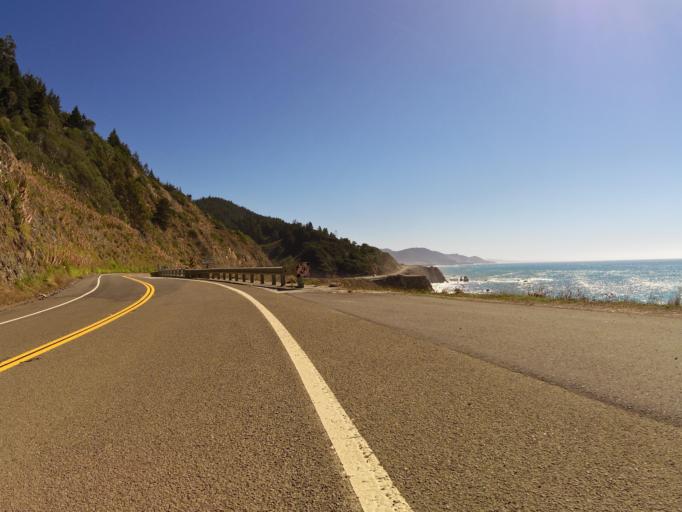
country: US
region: California
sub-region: Mendocino County
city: Fort Bragg
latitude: 39.7071
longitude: -123.8059
